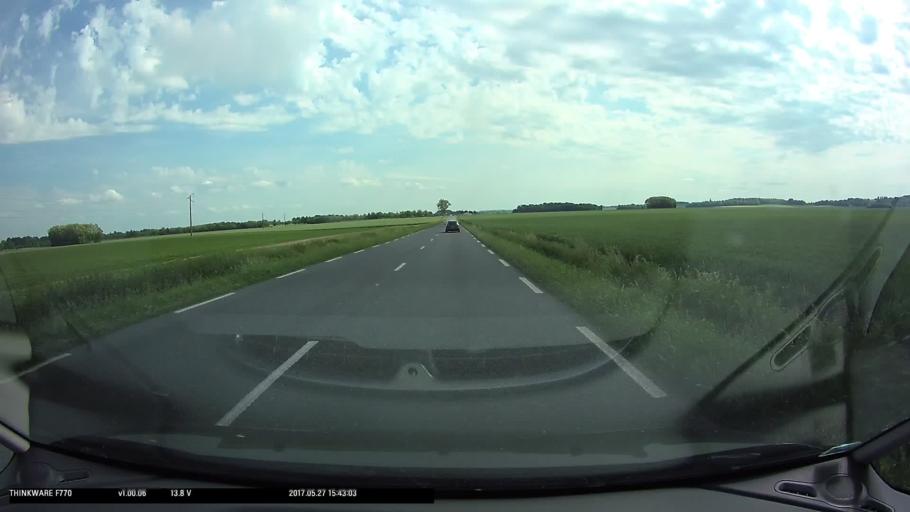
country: FR
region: Picardie
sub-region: Departement de l'Oise
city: Chaumont-en-Vexin
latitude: 49.2095
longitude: 1.8812
